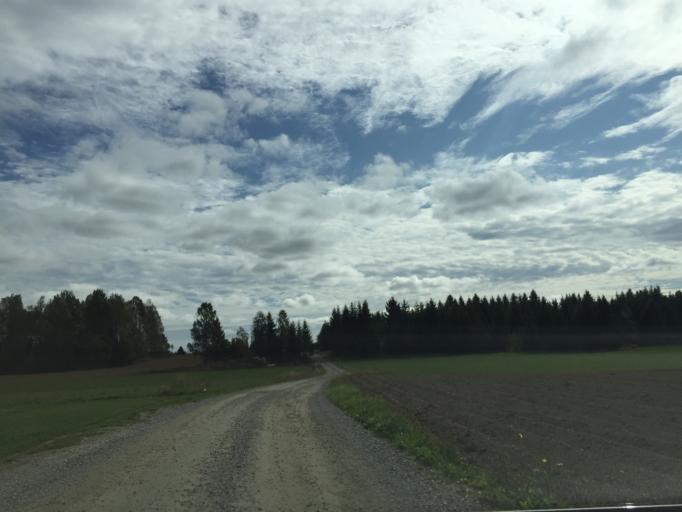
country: NO
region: Ostfold
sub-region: Hobol
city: Elvestad
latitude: 59.6316
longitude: 10.8906
